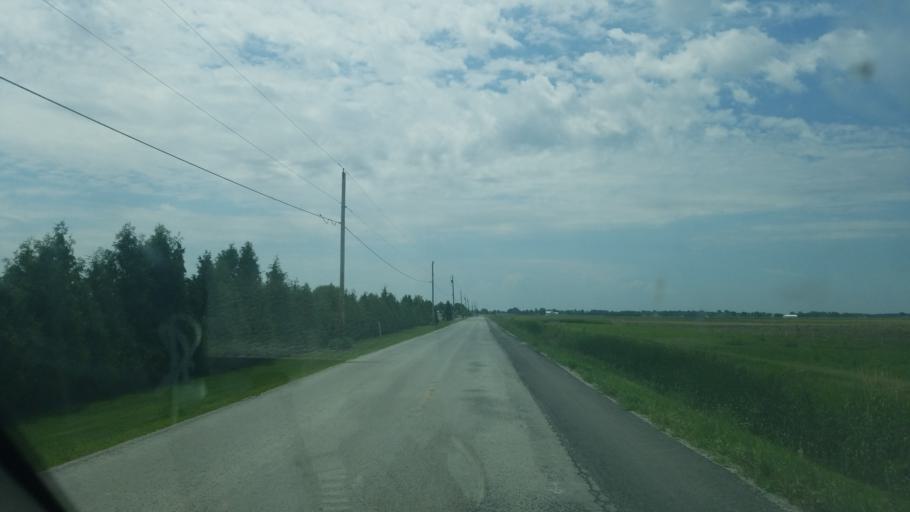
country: US
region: Ohio
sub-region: Wood County
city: Bowling Green
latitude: 41.2873
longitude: -83.5927
